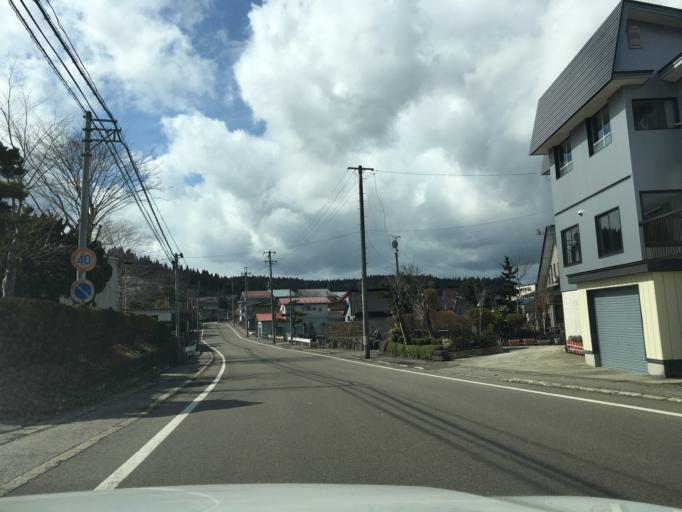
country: JP
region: Akita
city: Takanosu
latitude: 40.1196
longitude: 140.3721
